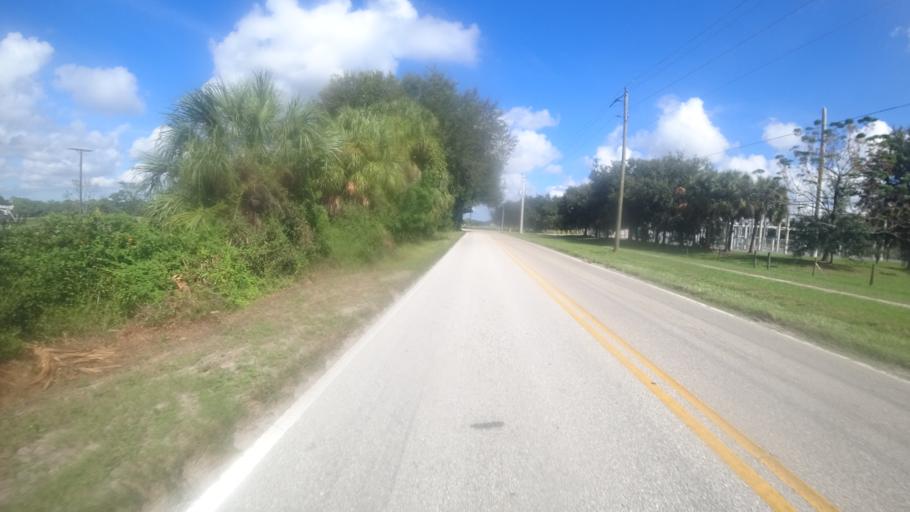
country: US
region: Florida
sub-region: Manatee County
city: Ellenton
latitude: 27.4755
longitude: -82.4566
